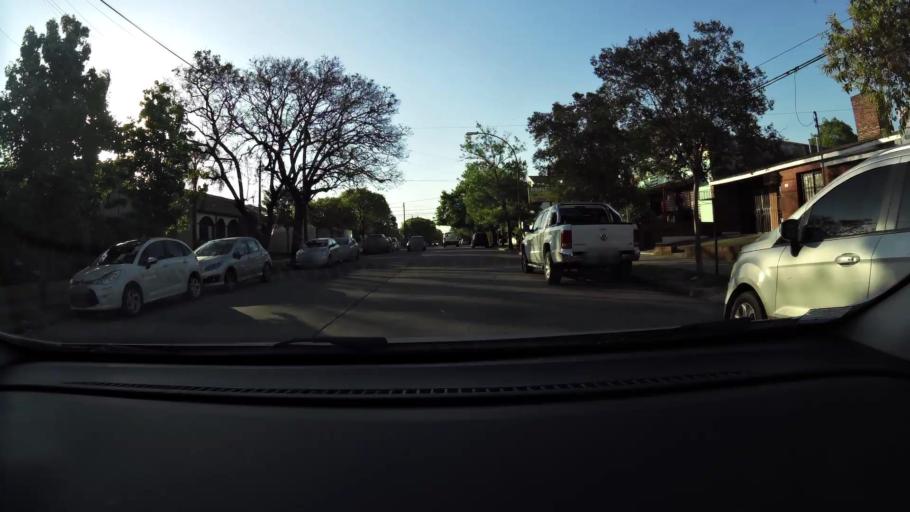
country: AR
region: Cordoba
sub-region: Departamento de Capital
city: Cordoba
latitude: -31.3815
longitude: -64.2408
